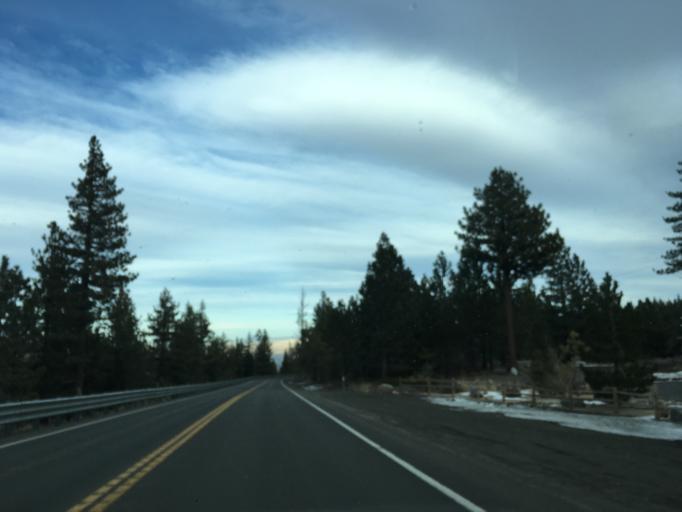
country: US
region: Nevada
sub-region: Washoe County
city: Incline Village
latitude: 39.3423
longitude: -119.8649
